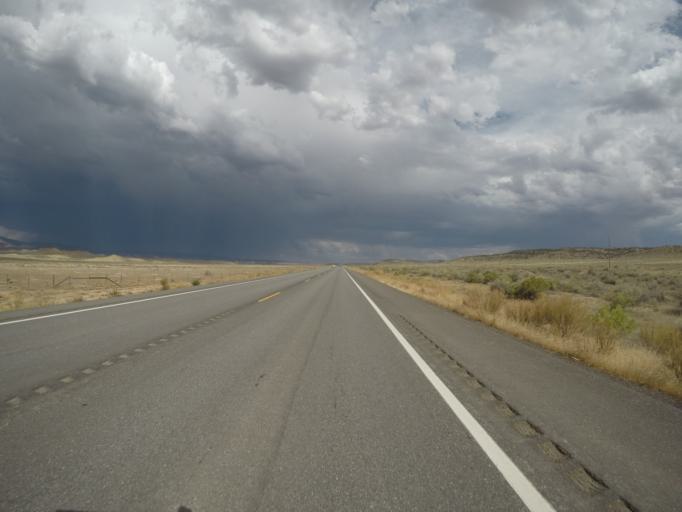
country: US
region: Utah
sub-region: Uintah County
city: Naples
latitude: 40.3003
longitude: -109.1937
